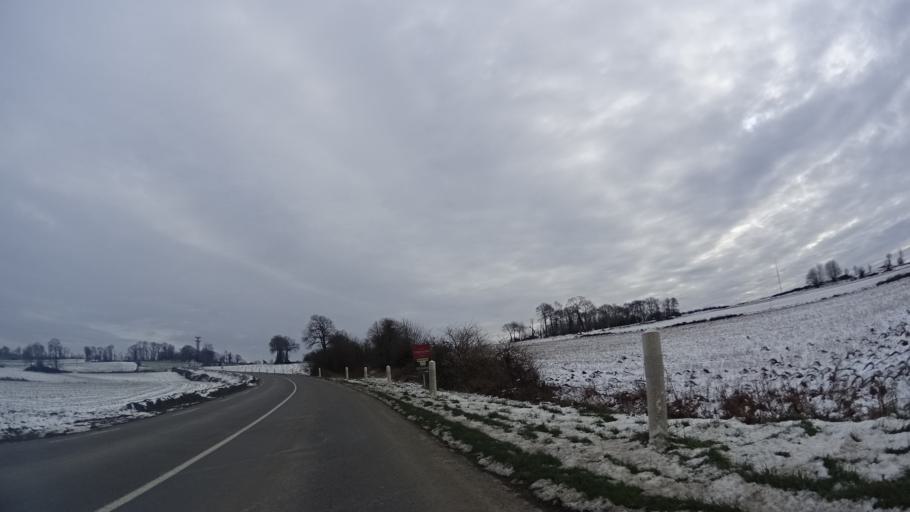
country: FR
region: Brittany
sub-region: Departement d'Ille-et-Vilaine
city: Irodouer
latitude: 48.3061
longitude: -1.9463
